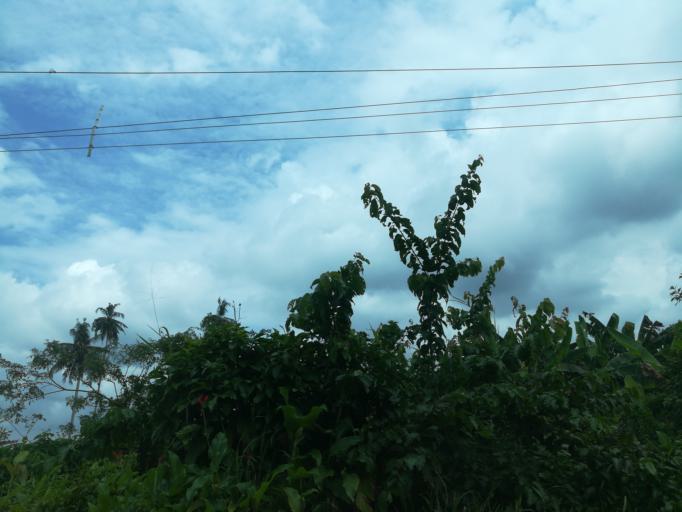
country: NG
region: Lagos
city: Ejirin
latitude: 6.6223
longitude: 3.7054
